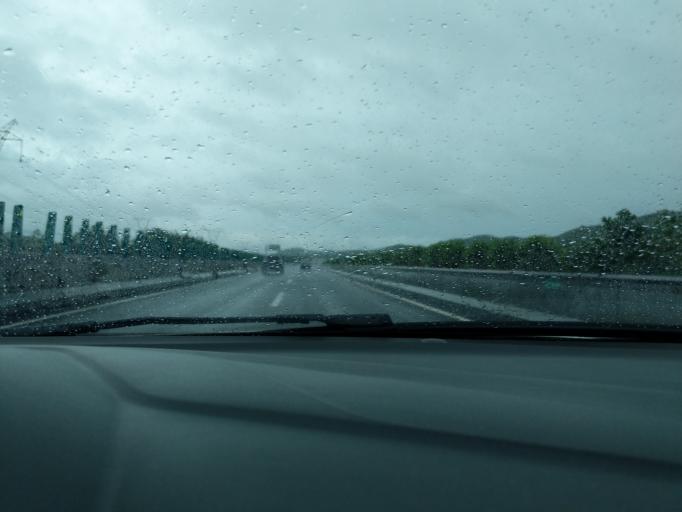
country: CN
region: Guangdong
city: Pingshi
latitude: 22.2625
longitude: 112.3171
